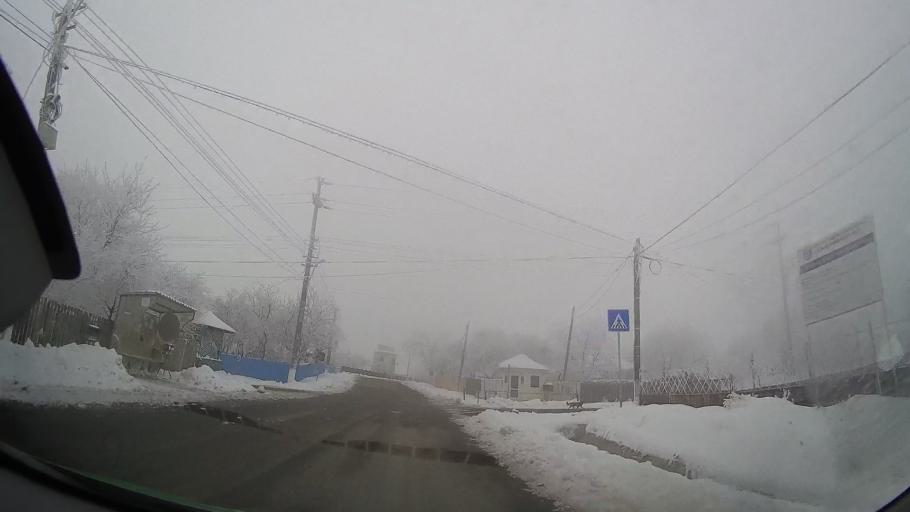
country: RO
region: Iasi
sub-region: Comuna Tansa
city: Suhulet
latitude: 46.8996
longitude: 27.2524
